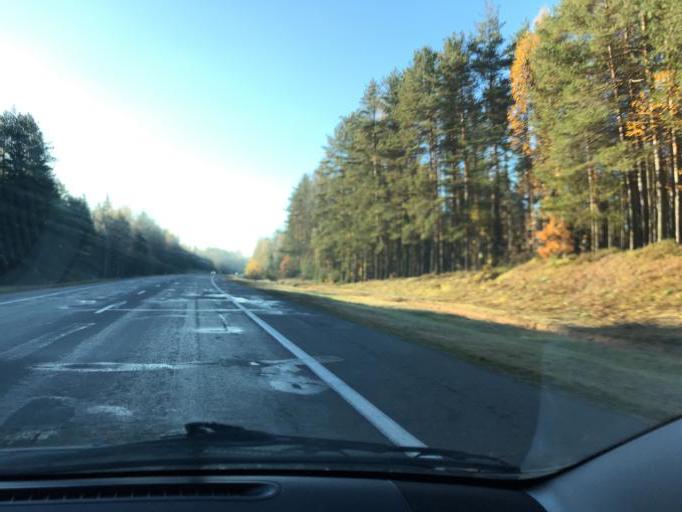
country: BY
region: Vitebsk
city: Vitebsk
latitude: 54.8889
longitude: 30.3869
